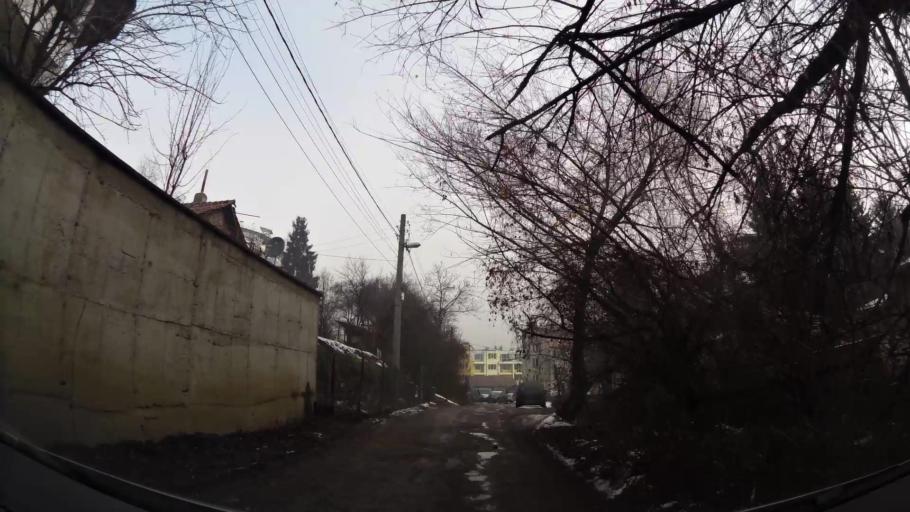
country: BG
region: Sofia-Capital
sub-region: Stolichna Obshtina
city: Sofia
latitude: 42.6590
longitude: 23.2631
